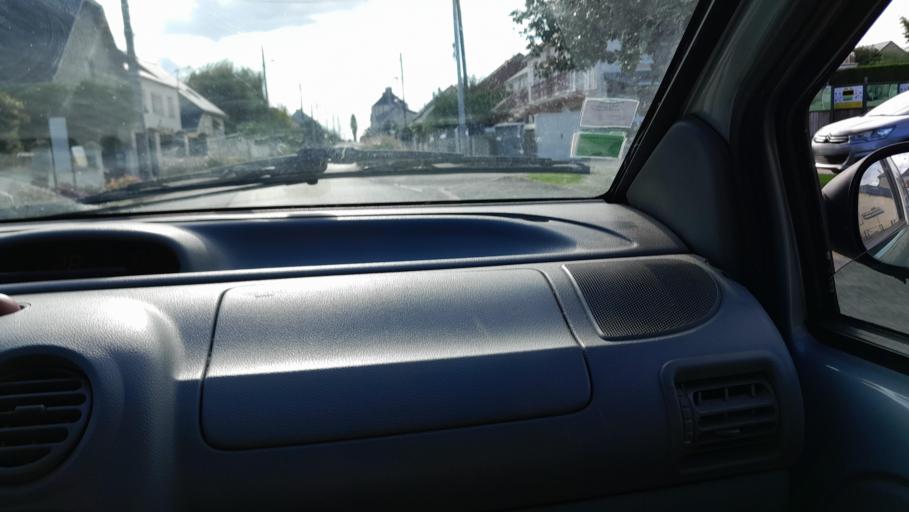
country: FR
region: Pays de la Loire
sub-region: Departement de la Mayenne
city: Loiron
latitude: 48.0048
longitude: -0.9627
